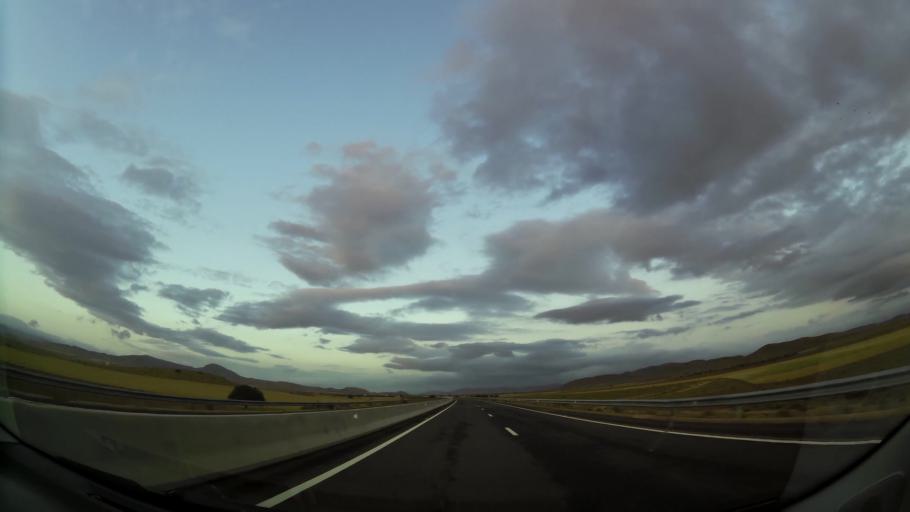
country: MA
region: Oriental
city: El Aioun
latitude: 34.5992
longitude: -2.7330
